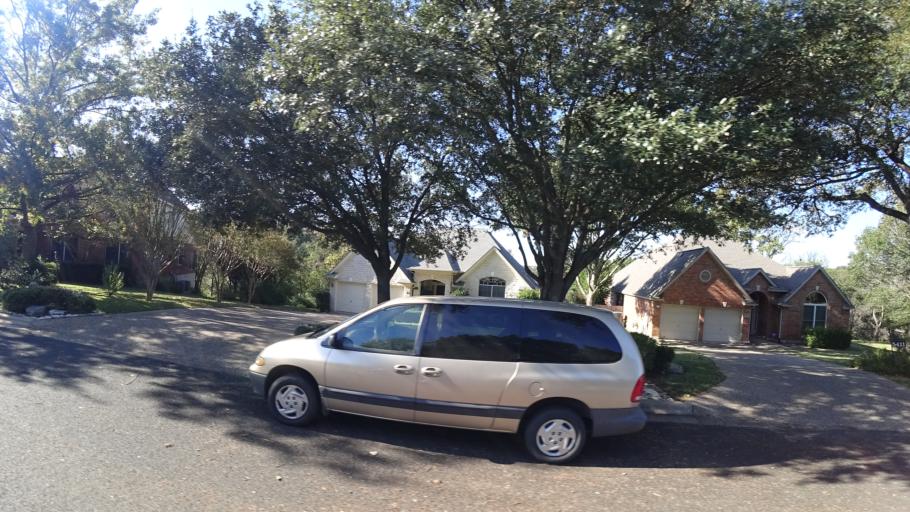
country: US
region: Texas
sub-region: Williamson County
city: Jollyville
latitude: 30.4070
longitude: -97.7531
